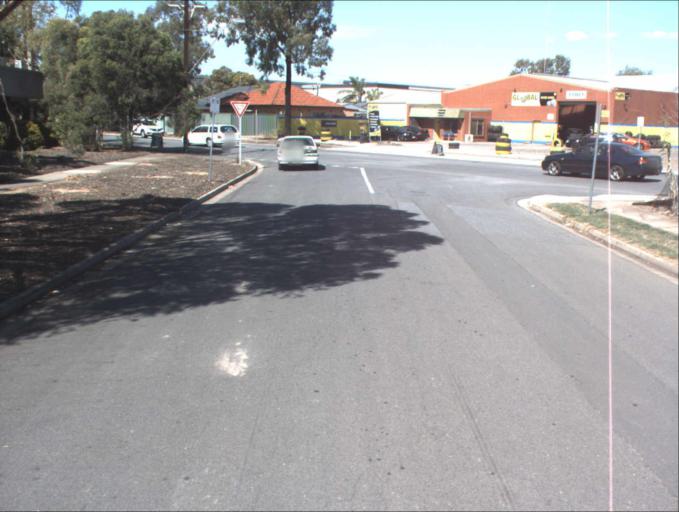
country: AU
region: South Australia
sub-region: Port Adelaide Enfield
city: Enfield
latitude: -34.8353
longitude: 138.5891
